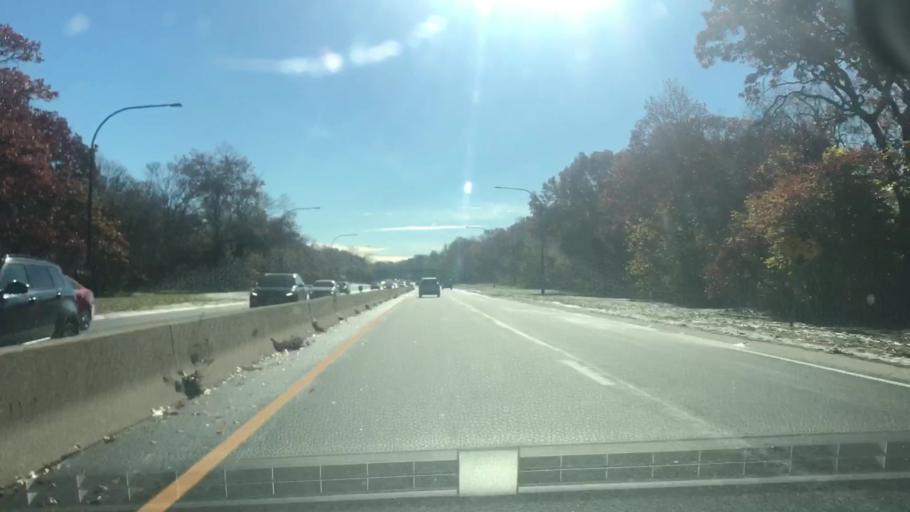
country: US
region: New York
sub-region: Nassau County
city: North Bellmore
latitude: 40.7107
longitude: -73.5280
